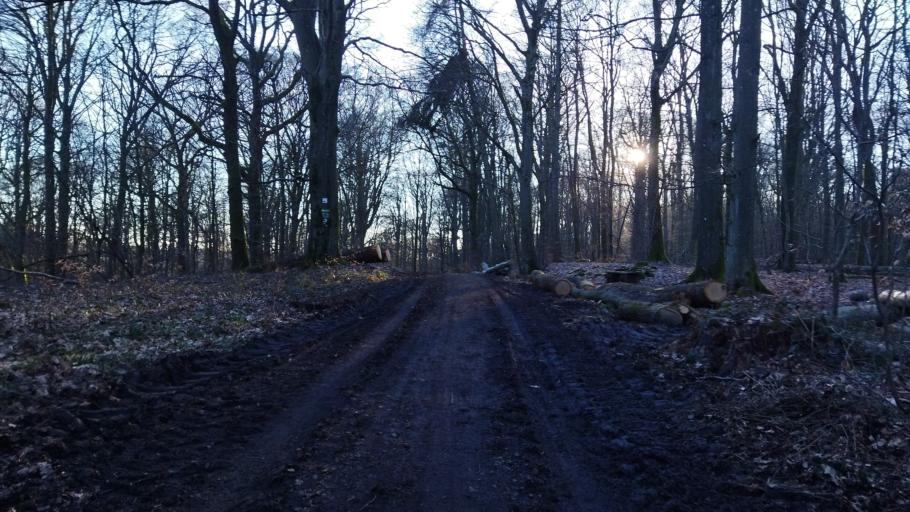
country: DE
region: Rheinland-Pfalz
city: Frohnhofen
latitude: 49.4621
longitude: 7.2888
